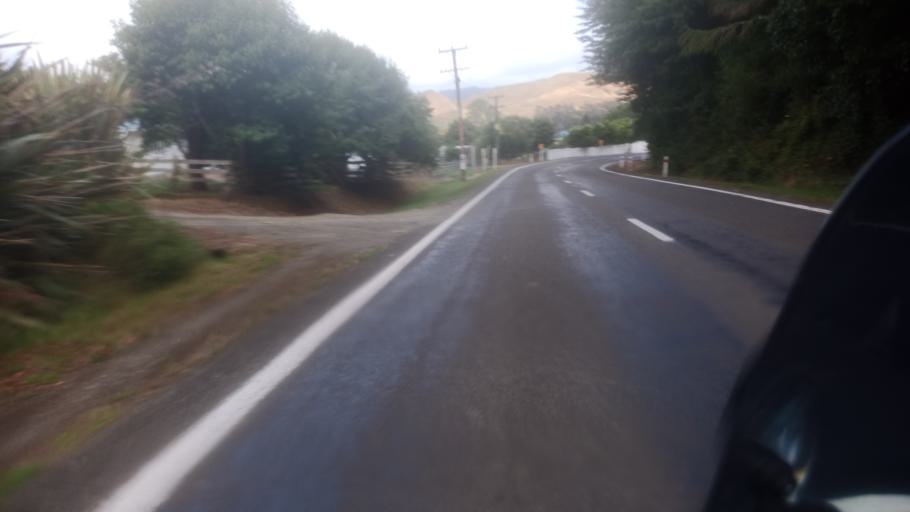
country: NZ
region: Bay of Plenty
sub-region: Opotiki District
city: Opotiki
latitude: -38.3588
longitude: 177.5375
